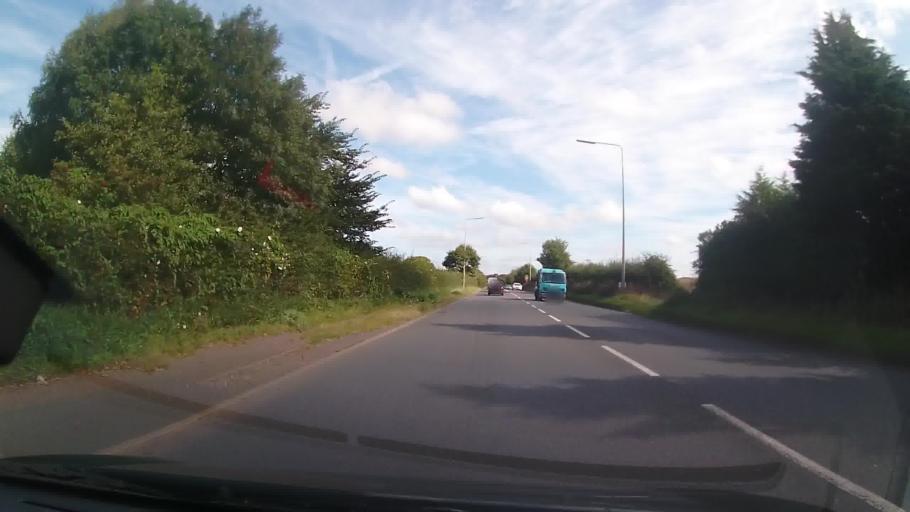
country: GB
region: England
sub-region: Staffordshire
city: Featherstone
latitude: 52.6553
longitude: -2.0739
